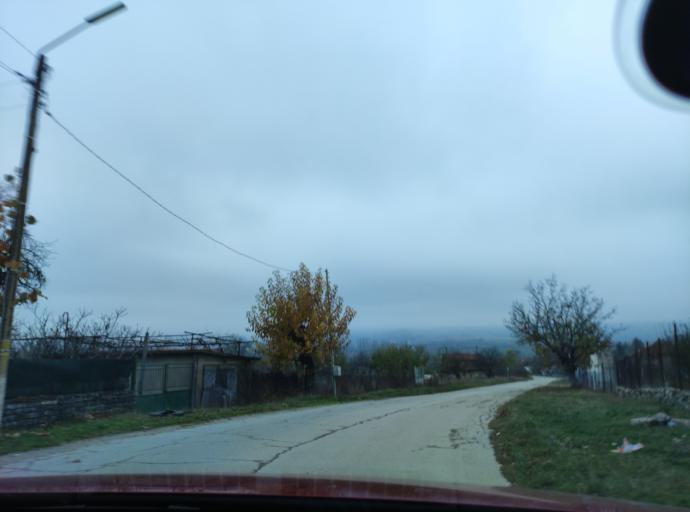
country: BG
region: Lovech
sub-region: Obshtina Yablanitsa
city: Yablanitsa
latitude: 43.0916
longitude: 24.0805
